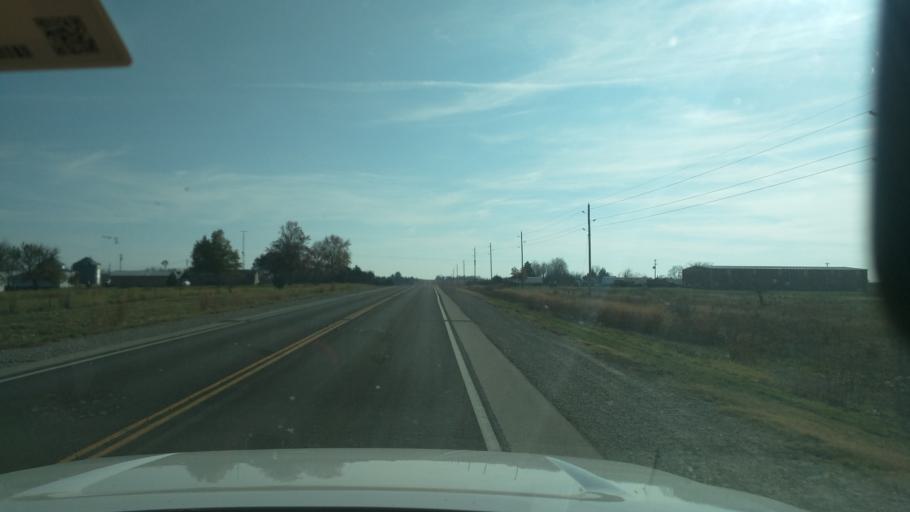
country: US
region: Kansas
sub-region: Lyon County
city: Emporia
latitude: 38.3494
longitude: -96.1803
